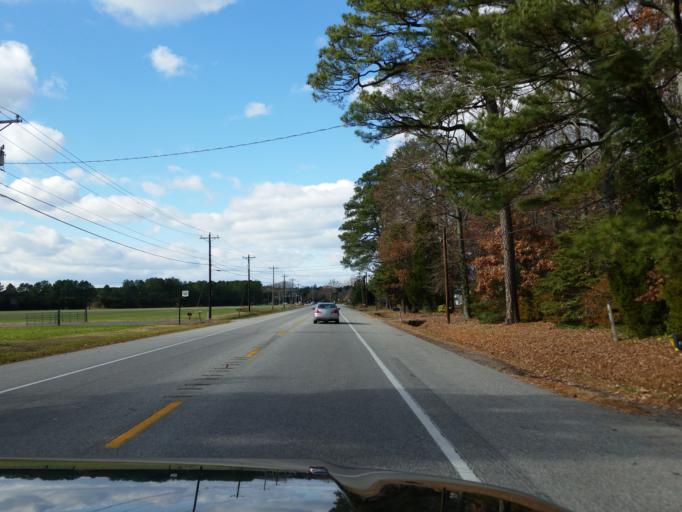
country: US
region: Maryland
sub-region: Talbot County
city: Easton
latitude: 38.7827
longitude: -76.1107
